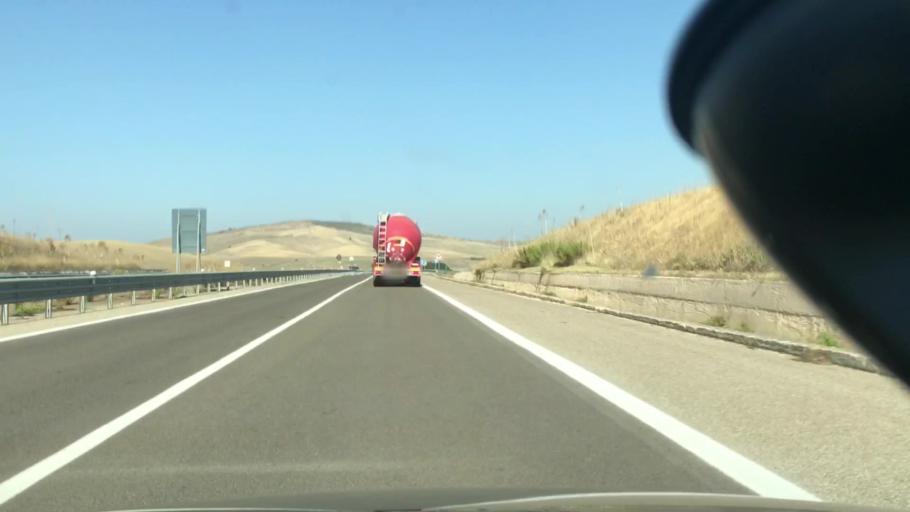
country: IT
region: Basilicate
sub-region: Provincia di Matera
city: Irsina
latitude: 40.7873
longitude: 16.2921
